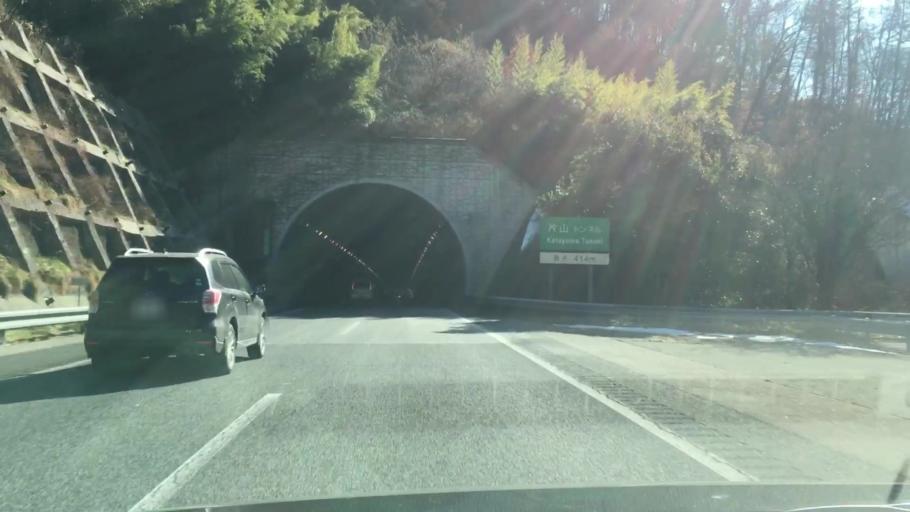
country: JP
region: Nagano
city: Ueda
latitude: 36.4774
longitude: 138.1928
